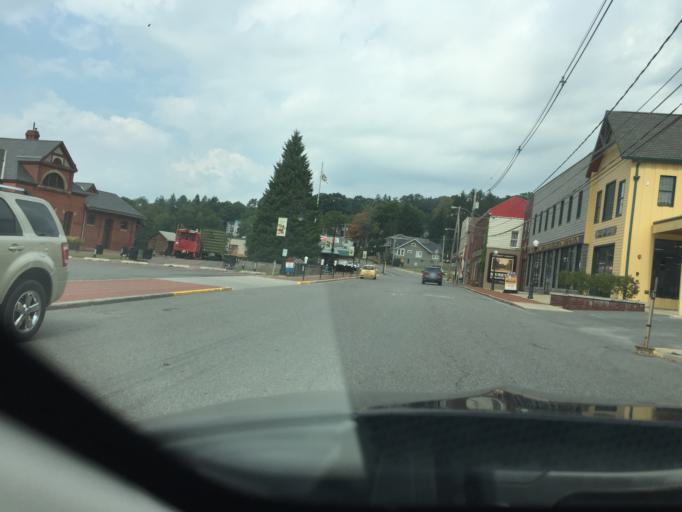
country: US
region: Maryland
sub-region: Garrett County
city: Oakland
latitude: 39.4096
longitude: -79.4082
